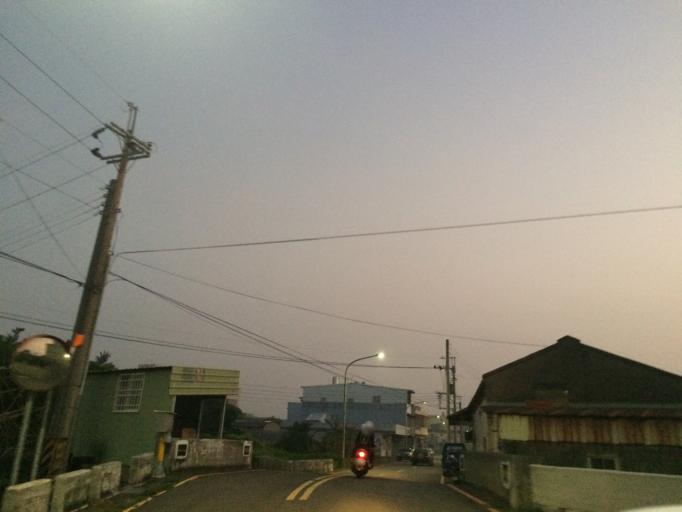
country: TW
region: Taiwan
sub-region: Hsinchu
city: Hsinchu
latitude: 24.7727
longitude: 120.9154
